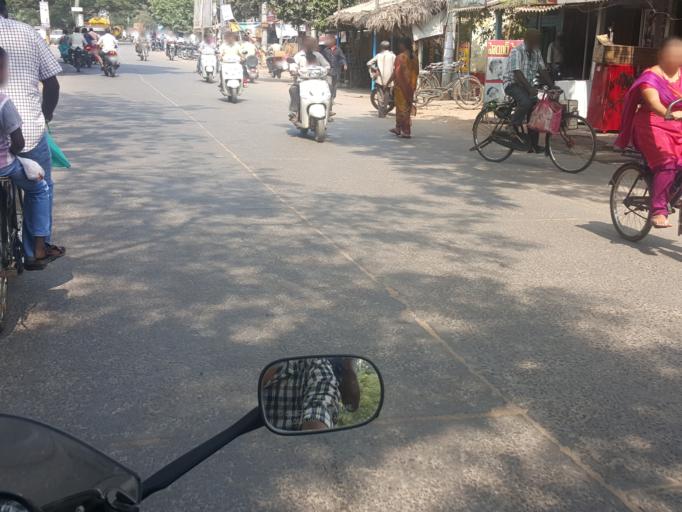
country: IN
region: Andhra Pradesh
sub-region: Guntur
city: Mangalagiri
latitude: 16.2425
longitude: 80.6496
